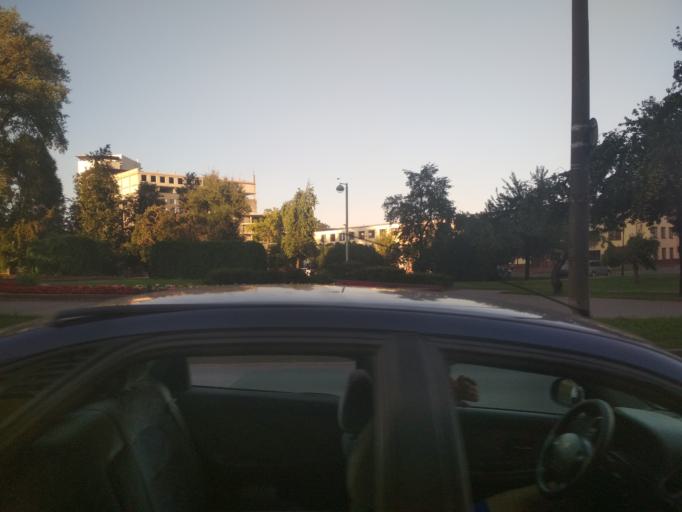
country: BY
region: Minsk
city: Minsk
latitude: 53.9023
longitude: 27.5829
